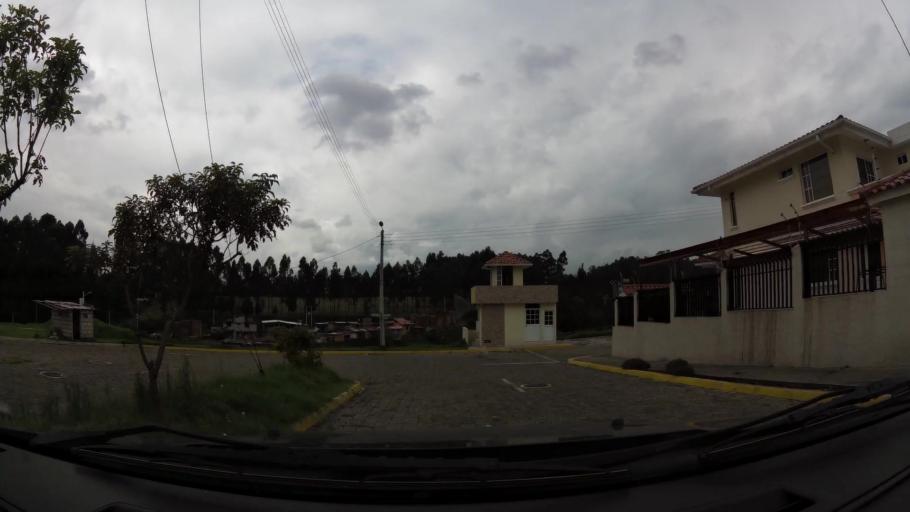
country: EC
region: Pichincha
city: Sangolqui
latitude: -0.3354
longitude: -78.4618
